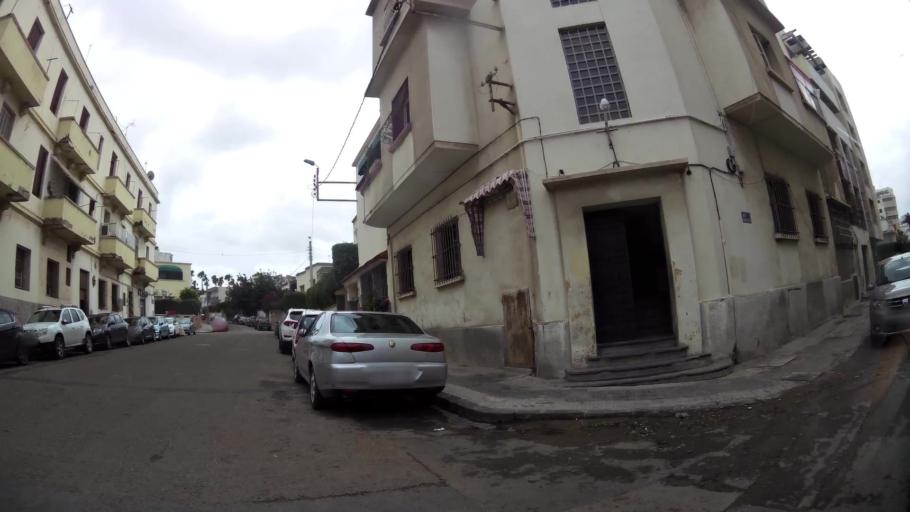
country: MA
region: Grand Casablanca
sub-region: Casablanca
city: Casablanca
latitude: 33.5830
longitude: -7.6129
